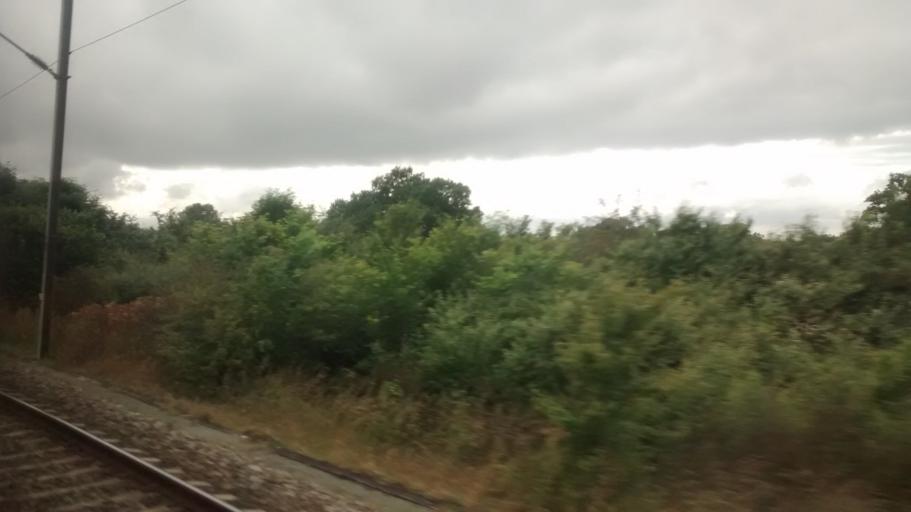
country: FR
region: Pays de la Loire
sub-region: Departement de la Mayenne
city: Evron
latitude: 48.1596
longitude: -0.4431
